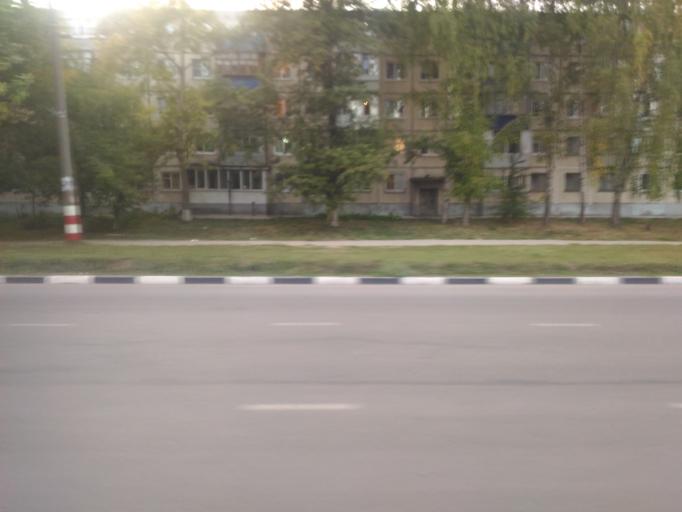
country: RU
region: Ulyanovsk
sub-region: Ulyanovskiy Rayon
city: Ulyanovsk
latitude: 54.2736
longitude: 48.2886
